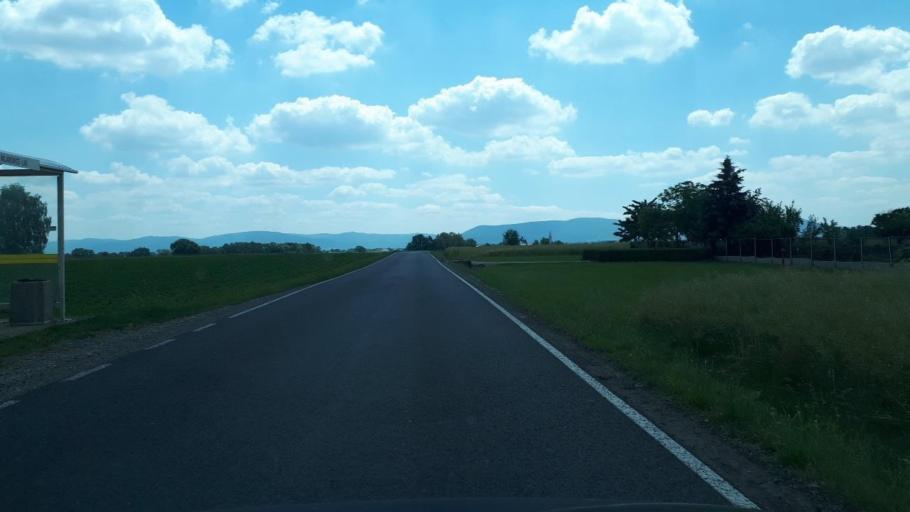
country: PL
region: Silesian Voivodeship
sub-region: Powiat bielski
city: Wilamowice
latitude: 49.9387
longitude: 19.1464
